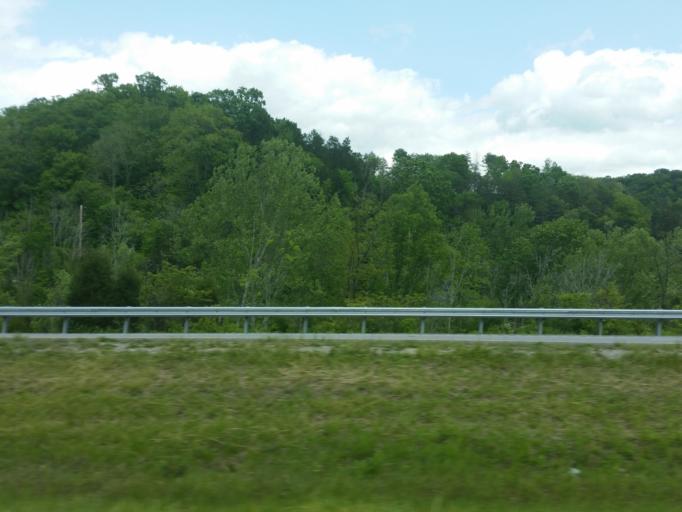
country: US
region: West Virginia
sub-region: Kanawha County
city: Sissonville
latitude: 38.5740
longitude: -81.6403
